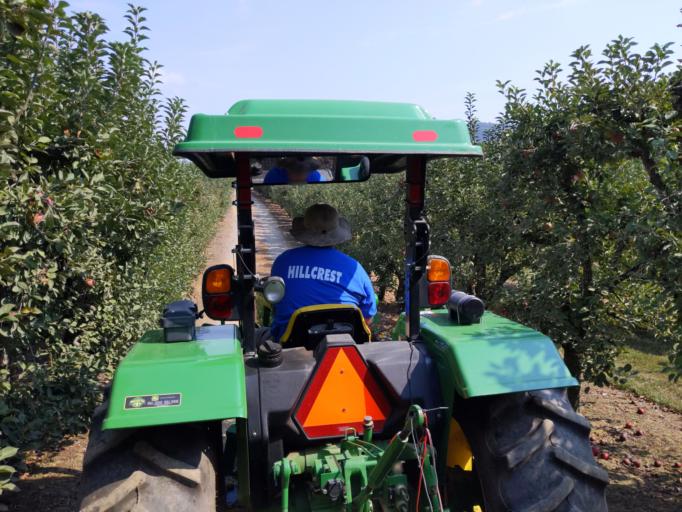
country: US
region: Georgia
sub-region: Gilmer County
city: Ellijay
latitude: 34.6186
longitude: -84.3746
